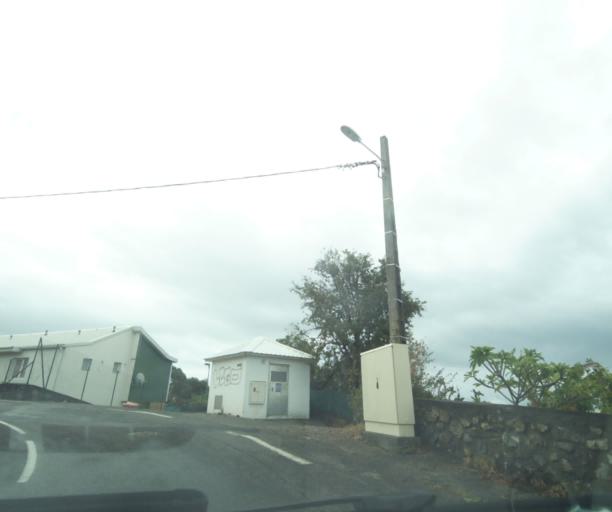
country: RE
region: Reunion
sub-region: Reunion
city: Saint-Paul
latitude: -21.0285
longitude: 55.2854
